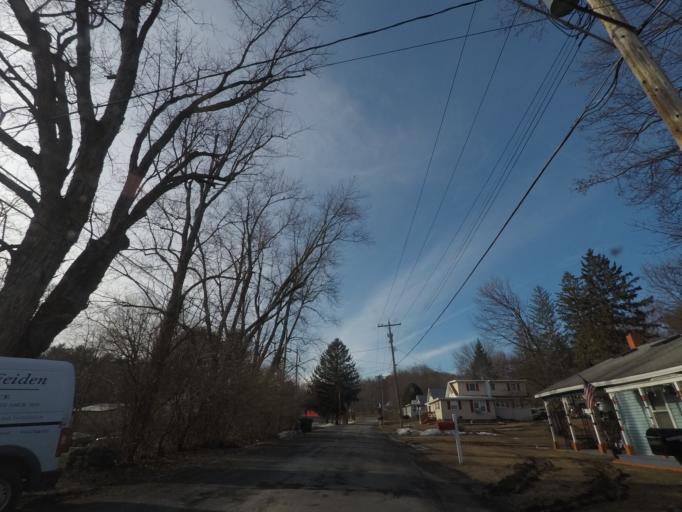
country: US
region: New York
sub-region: Rensselaer County
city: Nassau
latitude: 42.5451
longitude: -73.6051
